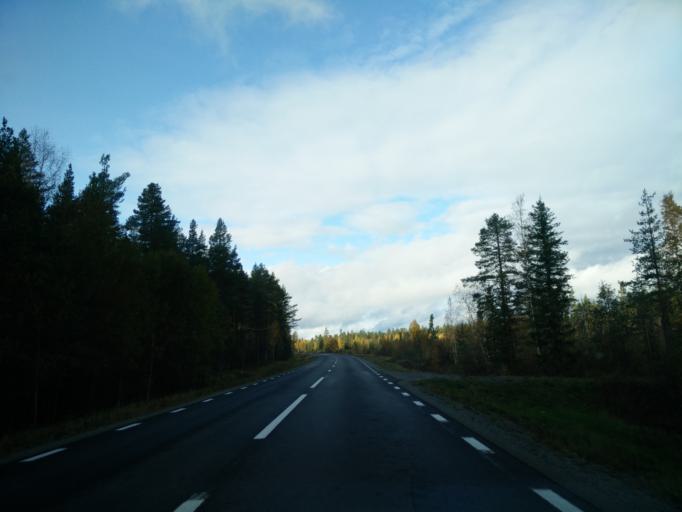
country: SE
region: Jaemtland
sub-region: Braecke Kommun
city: Braecke
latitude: 62.3876
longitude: 15.1196
